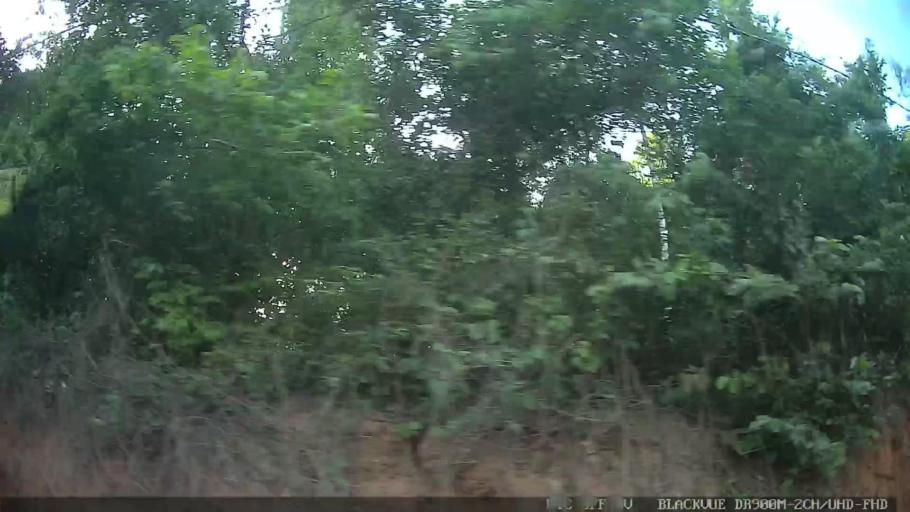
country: BR
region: Sao Paulo
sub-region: Amparo
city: Amparo
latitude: -22.6918
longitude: -46.6904
